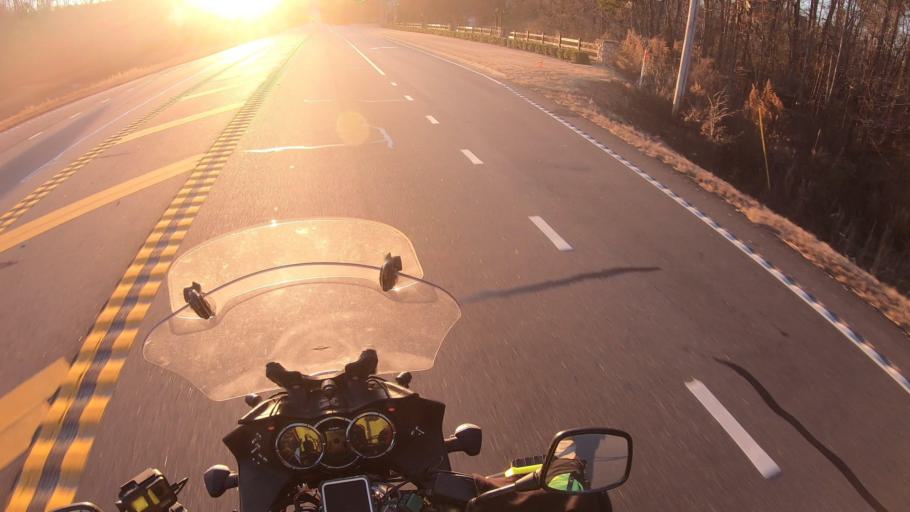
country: US
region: Georgia
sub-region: Forsyth County
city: Cumming
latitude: 34.2990
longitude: -84.2302
